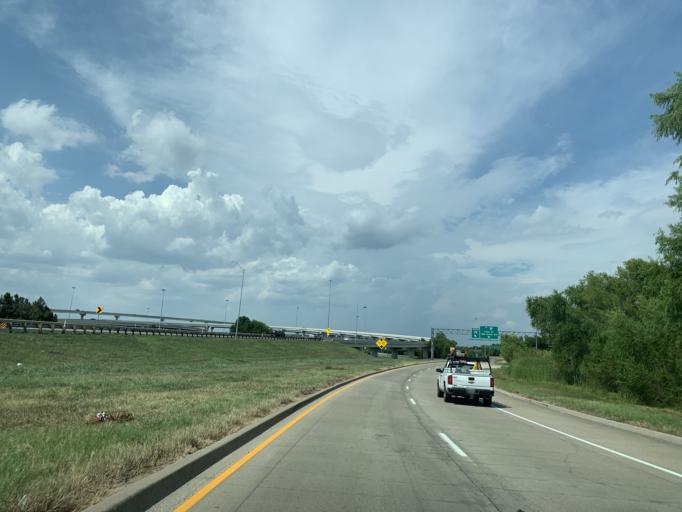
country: US
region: Texas
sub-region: Tarrant County
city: Edgecliff Village
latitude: 32.6619
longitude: -97.3204
